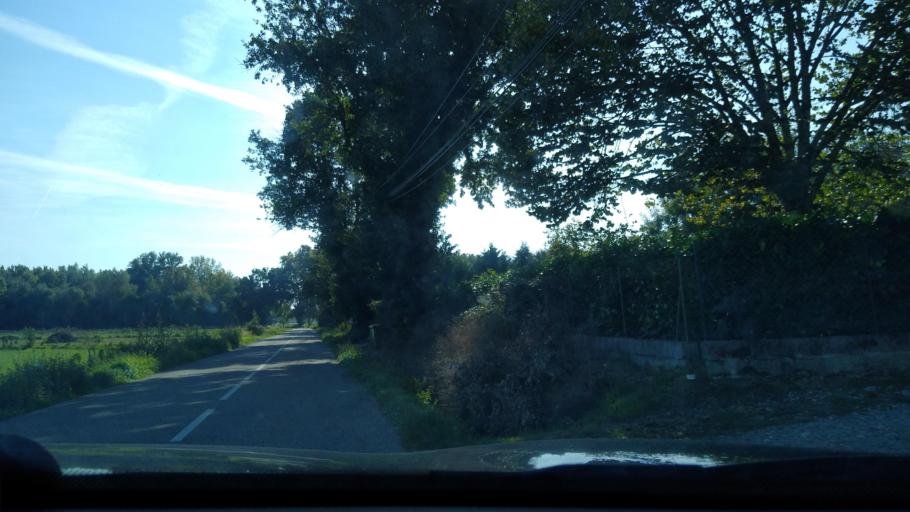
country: FR
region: Midi-Pyrenees
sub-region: Departement de la Haute-Garonne
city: Montaigut-sur-Save
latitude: 43.7308
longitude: 1.2387
